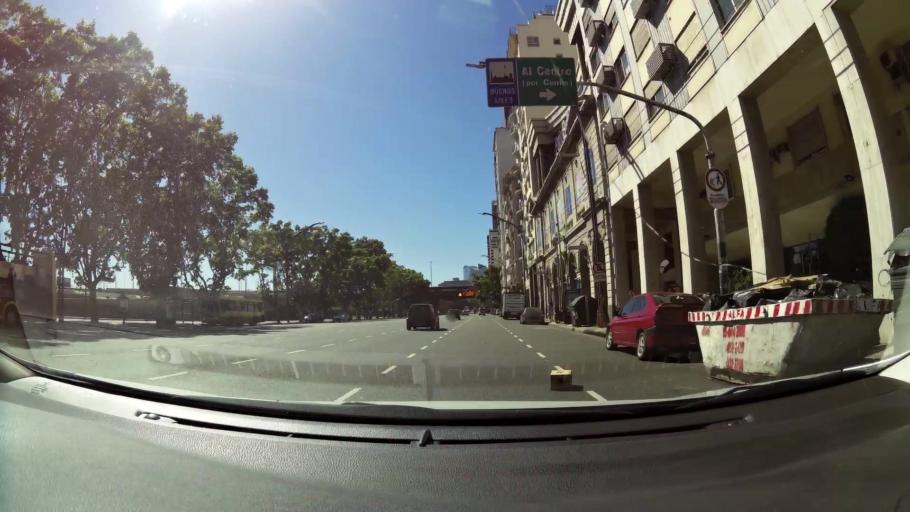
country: AR
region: Buenos Aires F.D.
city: Retiro
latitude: -34.5879
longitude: -58.3837
